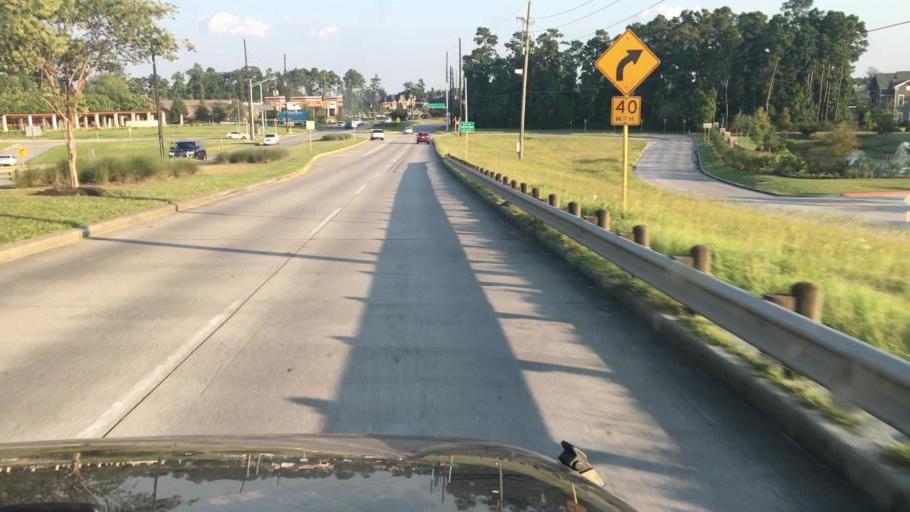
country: US
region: Texas
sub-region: Harris County
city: Atascocita
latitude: 29.9656
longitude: -95.1695
